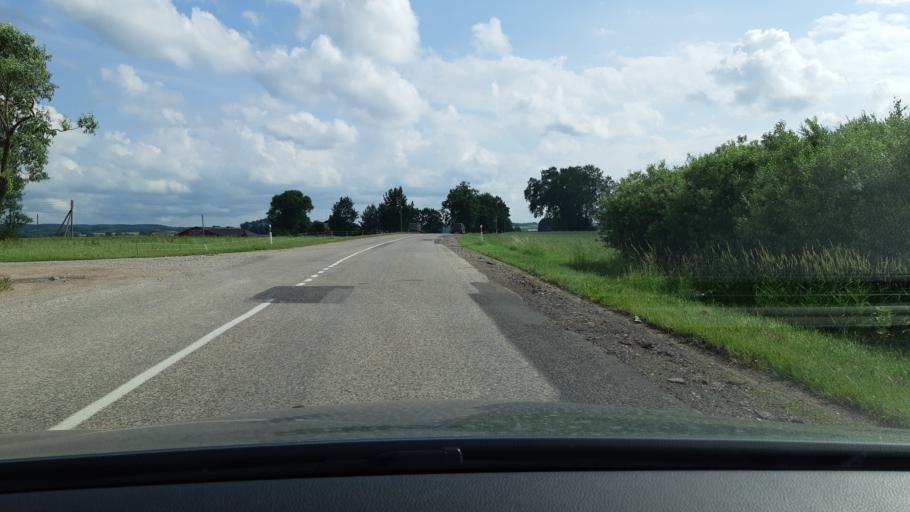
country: LT
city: Kybartai
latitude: 54.5696
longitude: 22.7241
